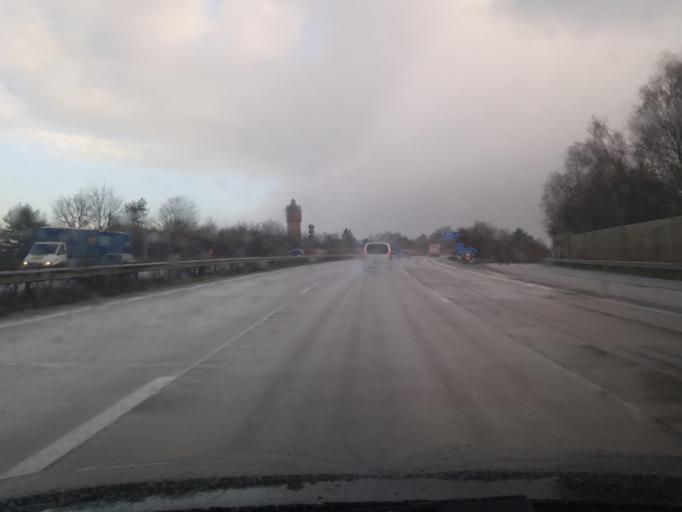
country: DE
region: Schleswig-Holstein
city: Bad Schwartau
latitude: 53.9045
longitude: 10.6851
